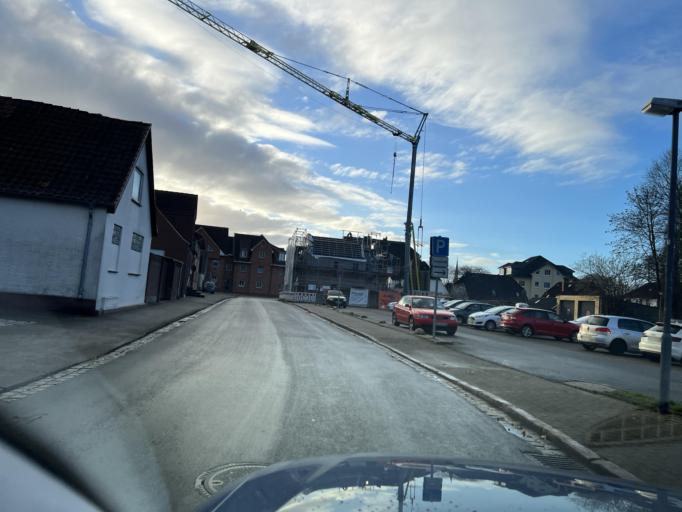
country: DE
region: Schleswig-Holstein
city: Heide
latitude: 54.1982
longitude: 9.0934
